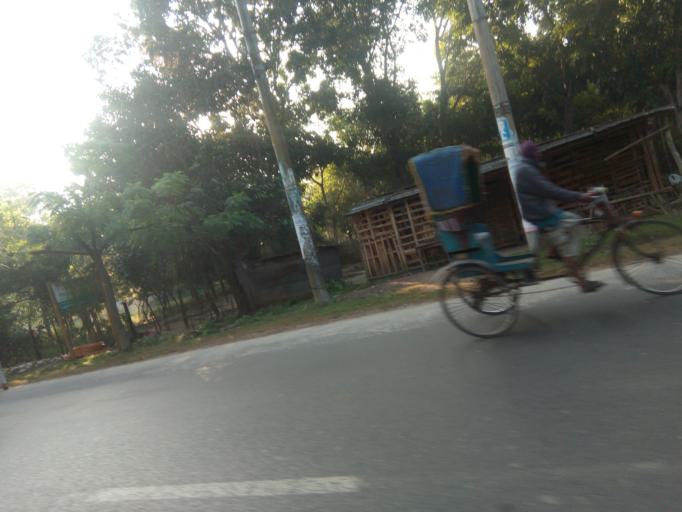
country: BD
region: Rajshahi
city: Rajshahi
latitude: 24.3656
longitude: 88.6355
